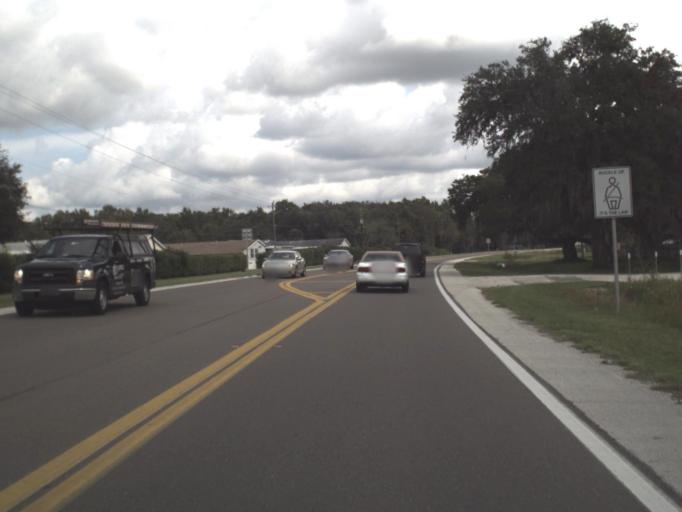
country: US
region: Florida
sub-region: Hendry County
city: LaBelle
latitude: 26.7839
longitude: -81.4370
